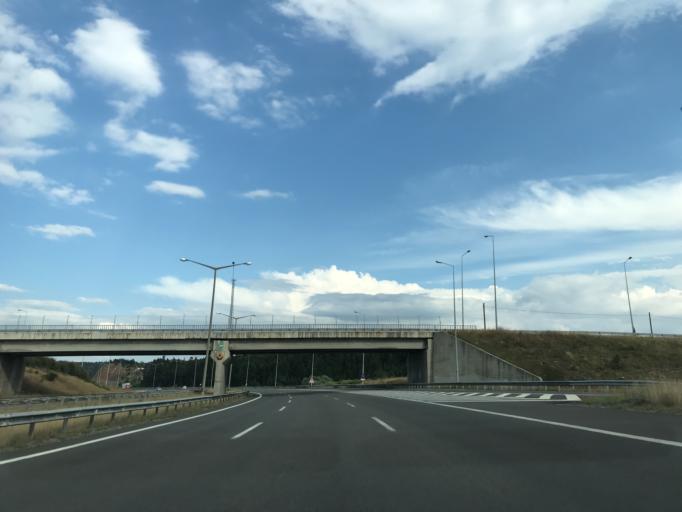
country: TR
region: Bolu
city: Gerede
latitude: 40.6126
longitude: 32.2517
